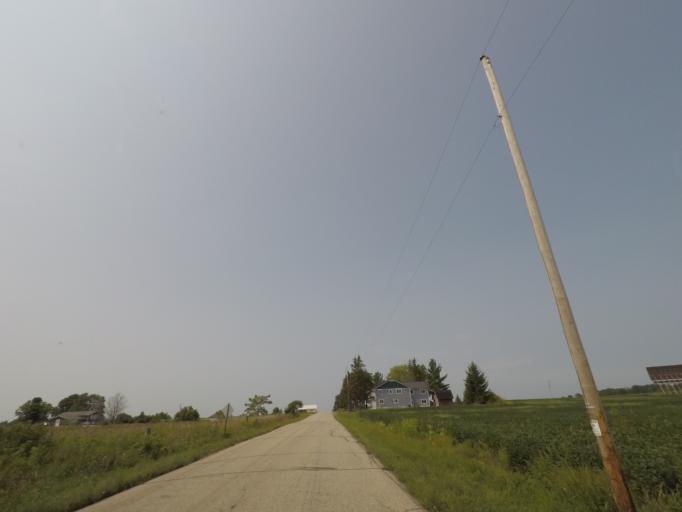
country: US
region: Wisconsin
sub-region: Waukesha County
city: Oconomowoc
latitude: 43.0664
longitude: -88.5579
